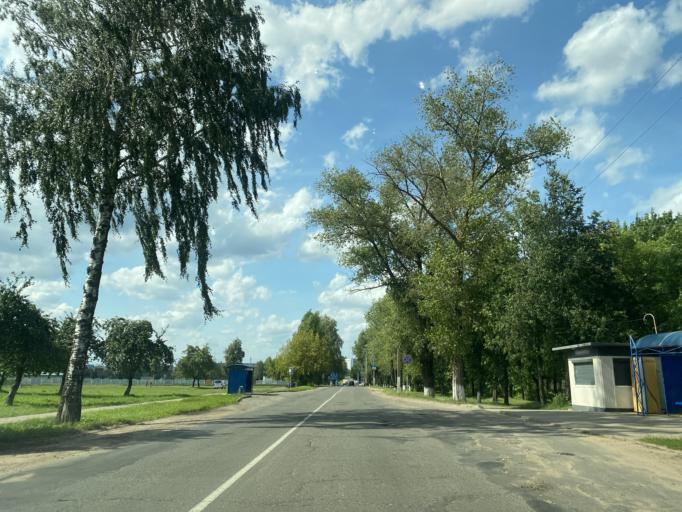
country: BY
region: Minsk
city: Horad Zhodzina
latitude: 54.0980
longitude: 28.3544
